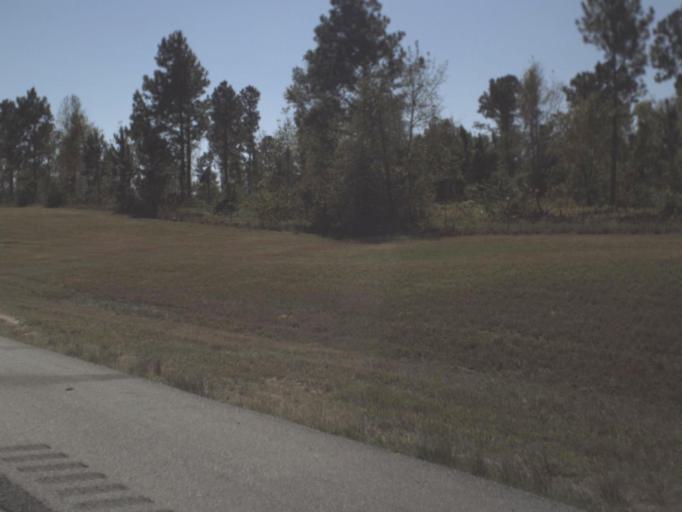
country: US
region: Florida
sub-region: Lake County
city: Minneola
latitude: 28.5967
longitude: -81.7172
